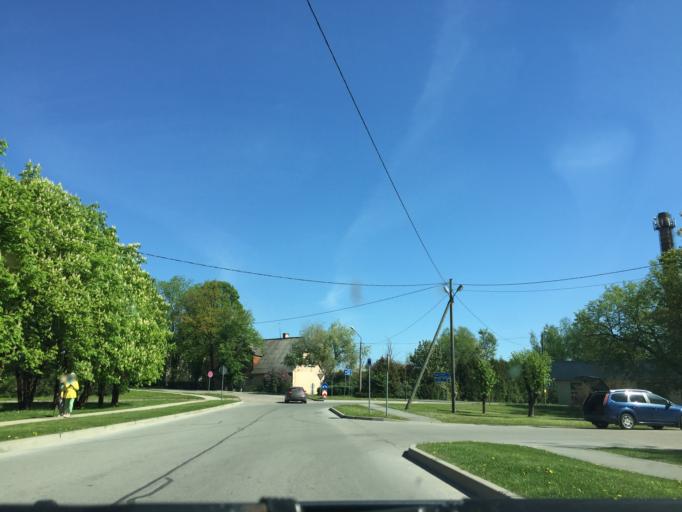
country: LV
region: Malpils
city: Malpils
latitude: 57.0114
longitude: 24.9572
